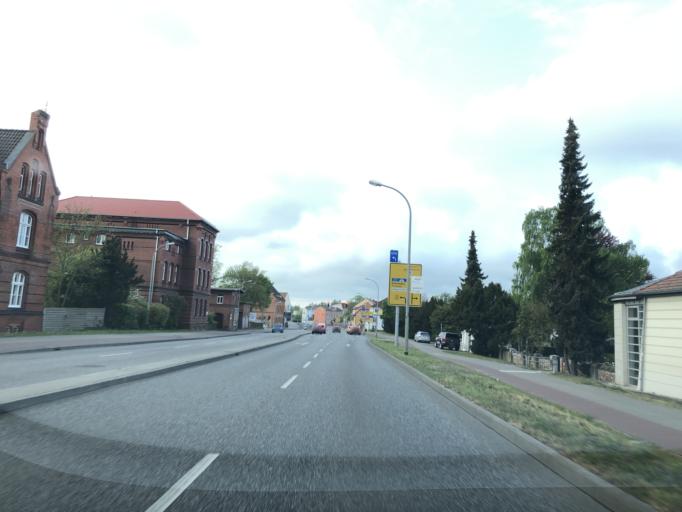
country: DE
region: Mecklenburg-Vorpommern
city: Guestrow
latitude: 53.8030
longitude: 12.1833
